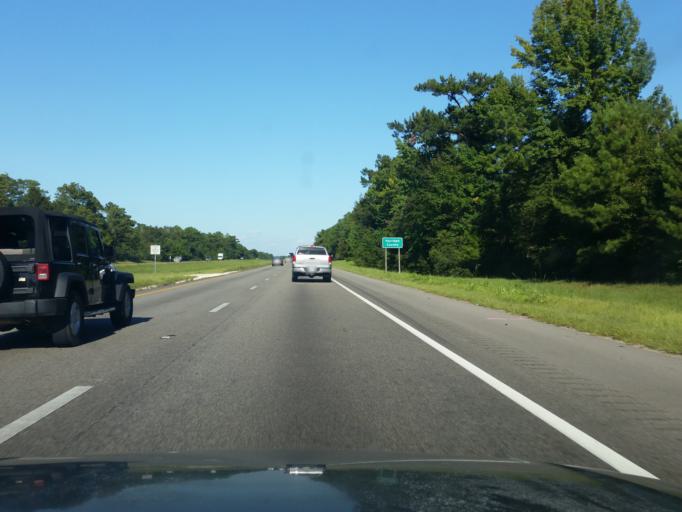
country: US
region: Mississippi
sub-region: Hancock County
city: Diamondhead
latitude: 30.3831
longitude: -89.3421
